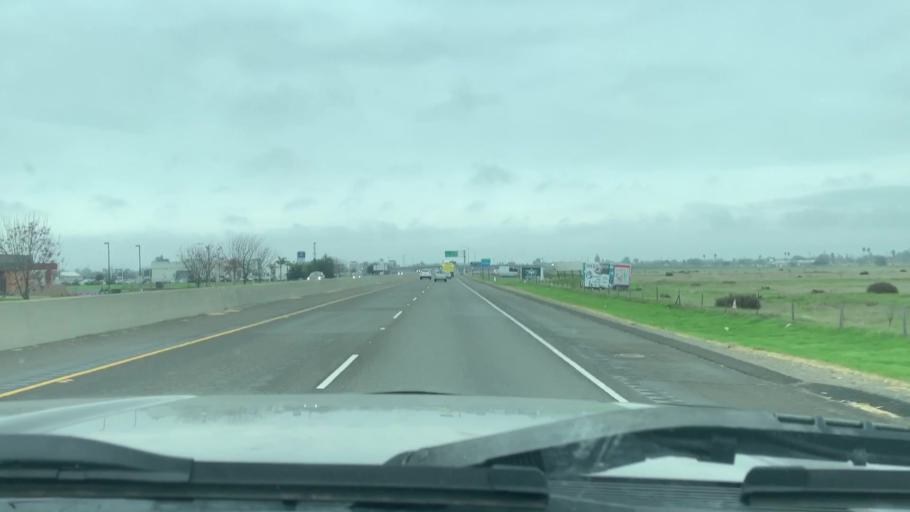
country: US
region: California
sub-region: Kings County
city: Armona
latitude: 36.3172
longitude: -119.6820
